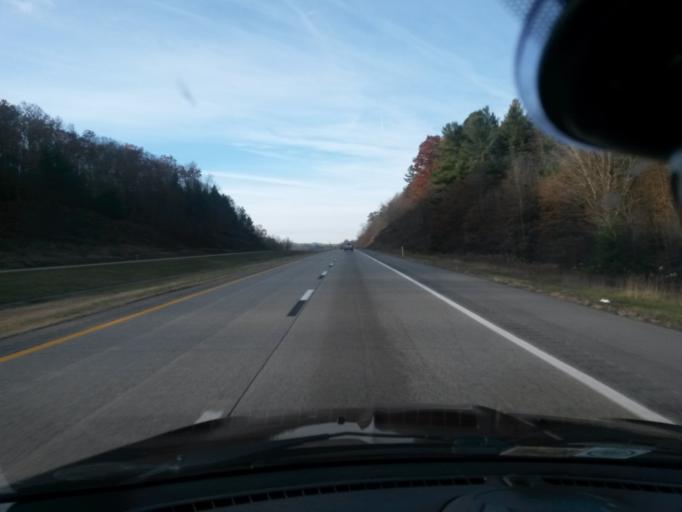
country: US
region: West Virginia
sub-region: Greenbrier County
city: Rainelle
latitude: 37.8800
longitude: -80.6838
